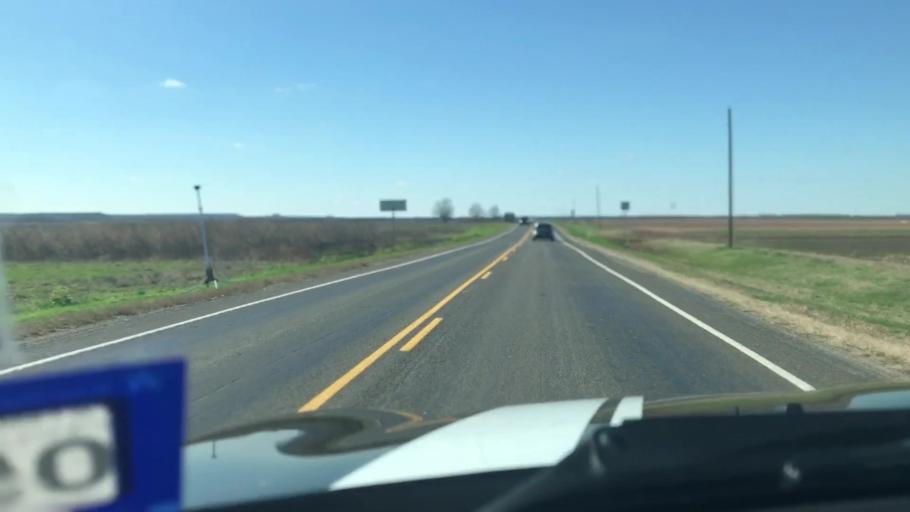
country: US
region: Texas
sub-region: Robertson County
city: Hearne
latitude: 30.8724
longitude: -96.6624
